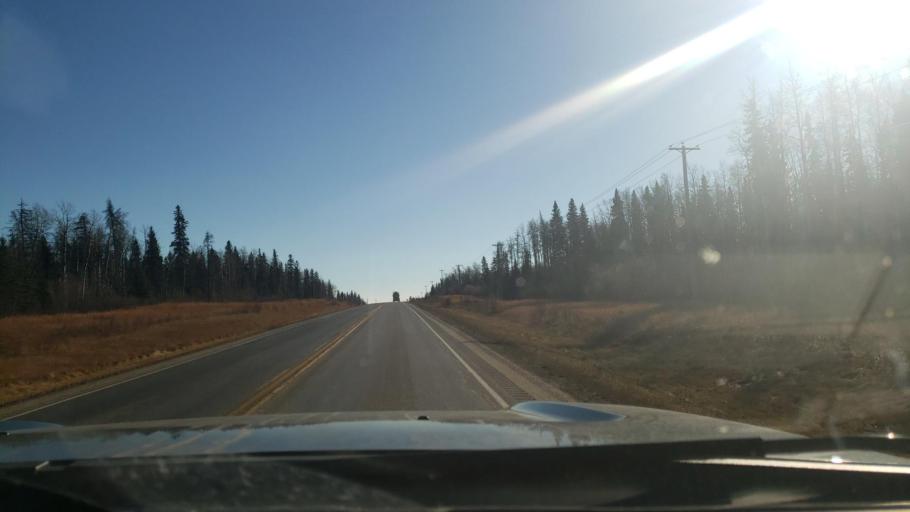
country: CA
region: British Columbia
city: Fort St. John
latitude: 56.6551
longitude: -121.6663
